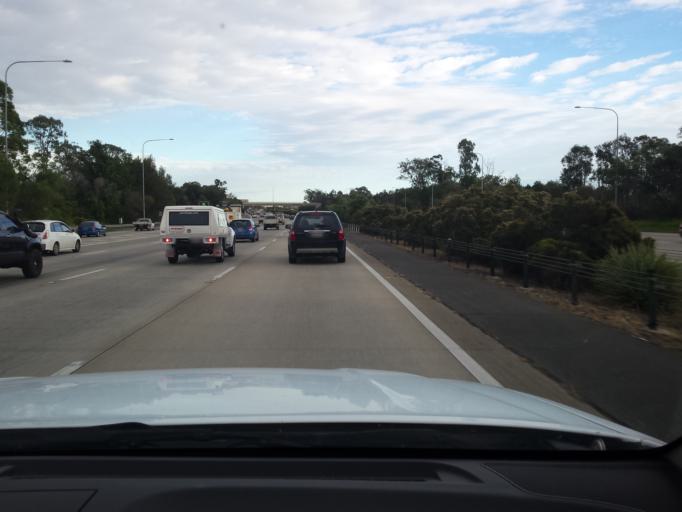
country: AU
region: Queensland
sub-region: Gold Coast
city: Ormeau Hills
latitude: -27.7614
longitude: 153.2457
